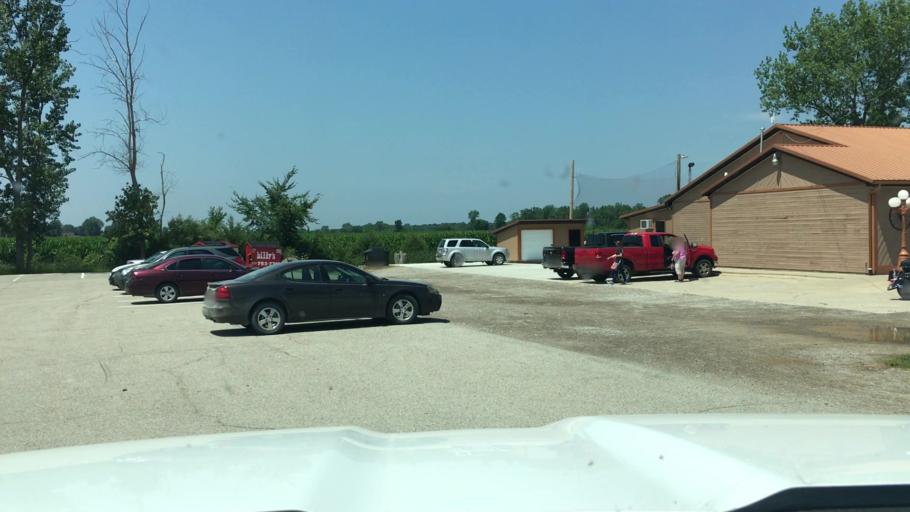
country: US
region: Michigan
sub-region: Saginaw County
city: Chesaning
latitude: 43.1872
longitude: -84.1691
